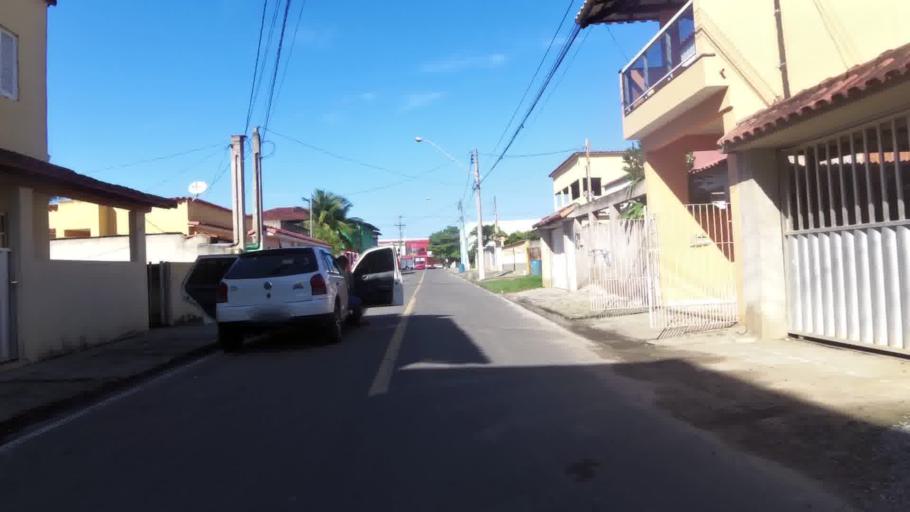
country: BR
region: Espirito Santo
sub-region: Piuma
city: Piuma
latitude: -20.8072
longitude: -40.6403
